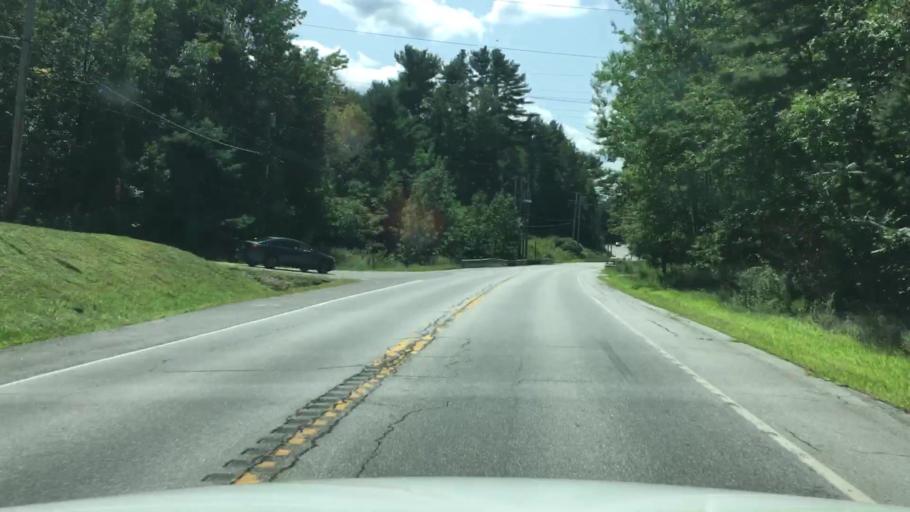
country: US
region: Maine
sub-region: Kennebec County
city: Farmingdale
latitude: 44.2547
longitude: -69.7654
